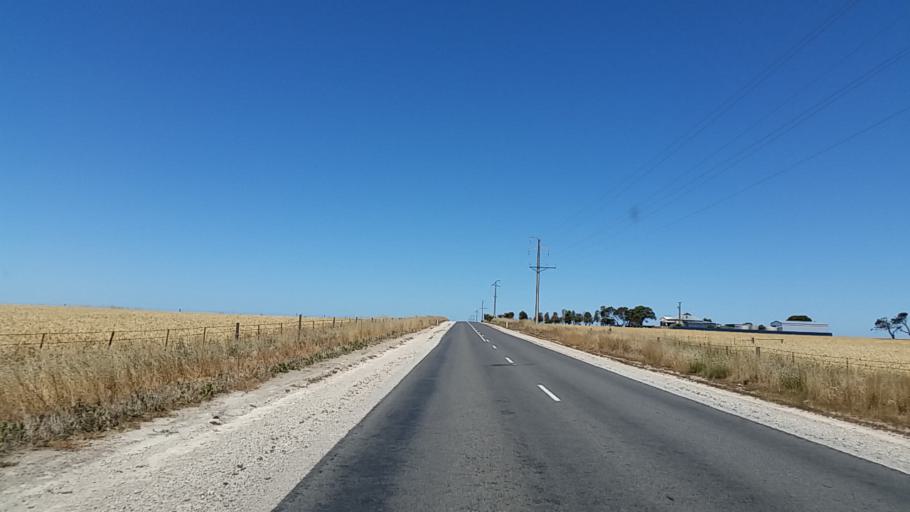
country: AU
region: South Australia
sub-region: Yorke Peninsula
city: Honiton
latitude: -35.0135
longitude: 137.6364
